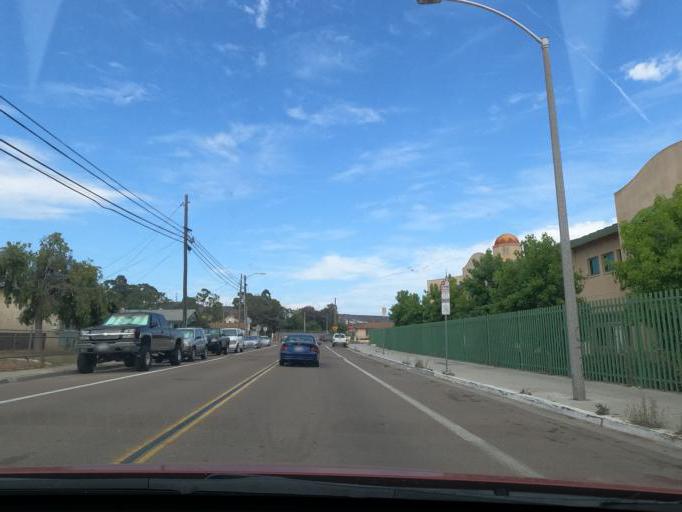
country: US
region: California
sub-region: San Diego County
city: Imperial Beach
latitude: 32.5582
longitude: -117.0503
